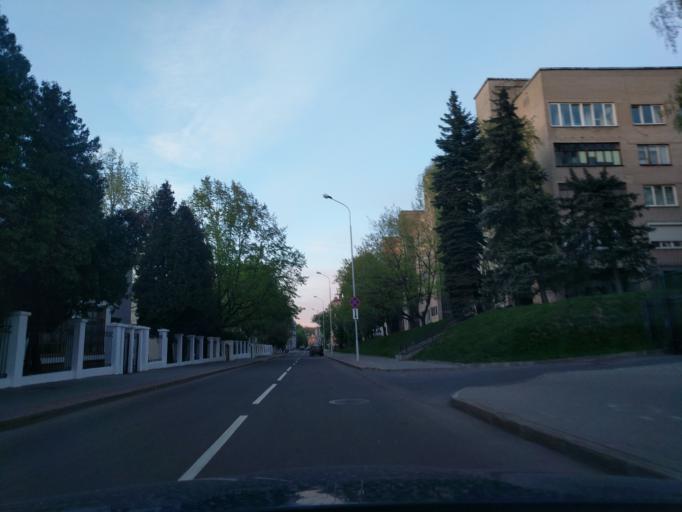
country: BY
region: Minsk
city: Minsk
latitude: 53.9040
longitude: 27.5773
